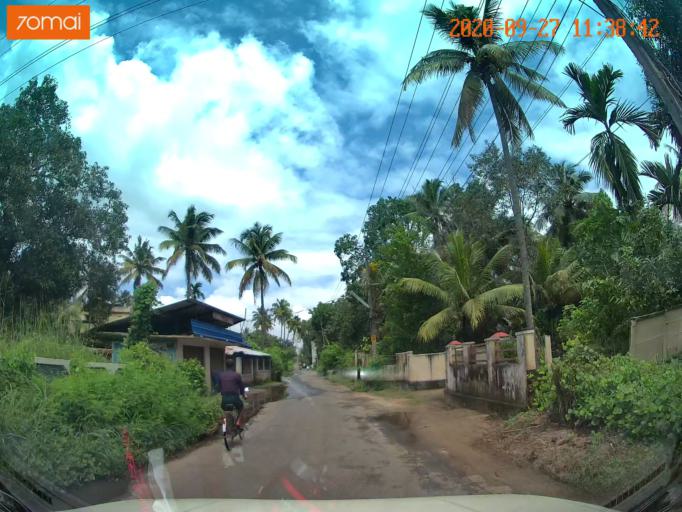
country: IN
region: Kerala
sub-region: Thrissur District
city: Thanniyam
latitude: 10.4612
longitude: 76.1203
